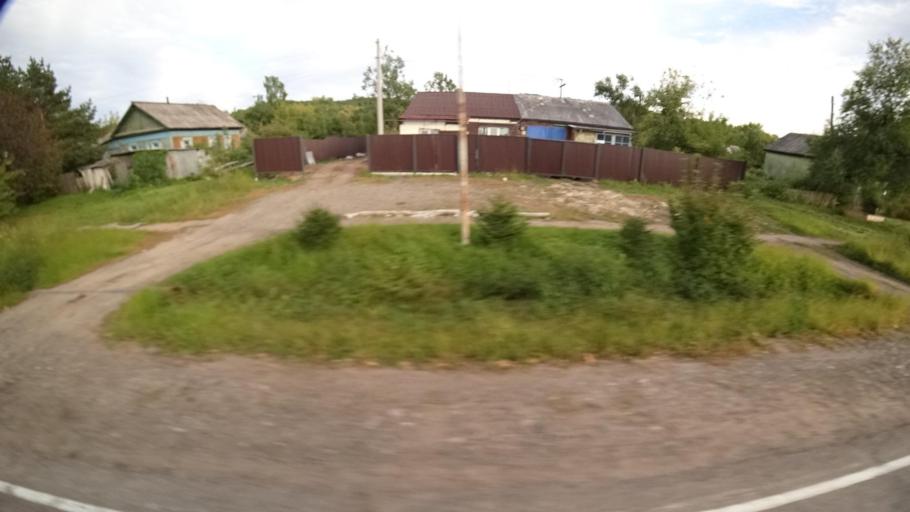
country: RU
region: Primorskiy
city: Yakovlevka
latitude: 44.4200
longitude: 133.4563
